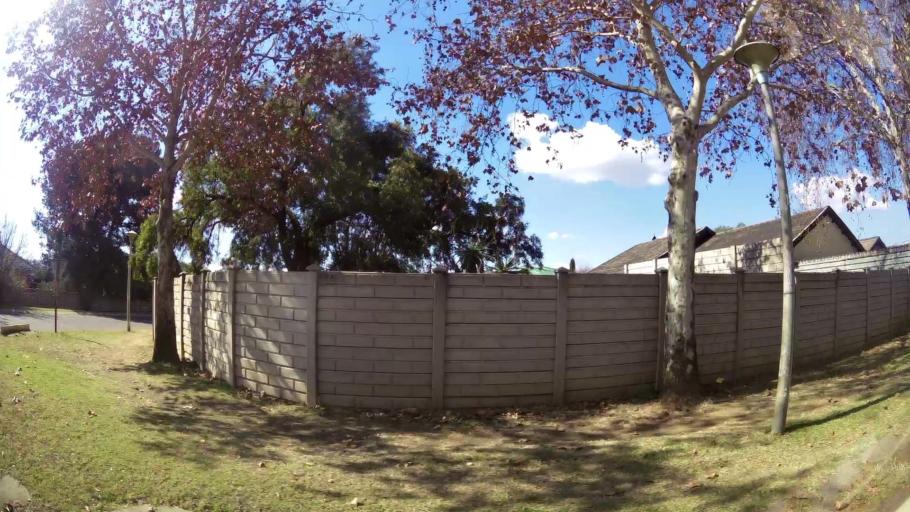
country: ZA
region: Mpumalanga
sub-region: Nkangala District Municipality
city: Witbank
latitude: -25.9444
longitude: 29.2452
